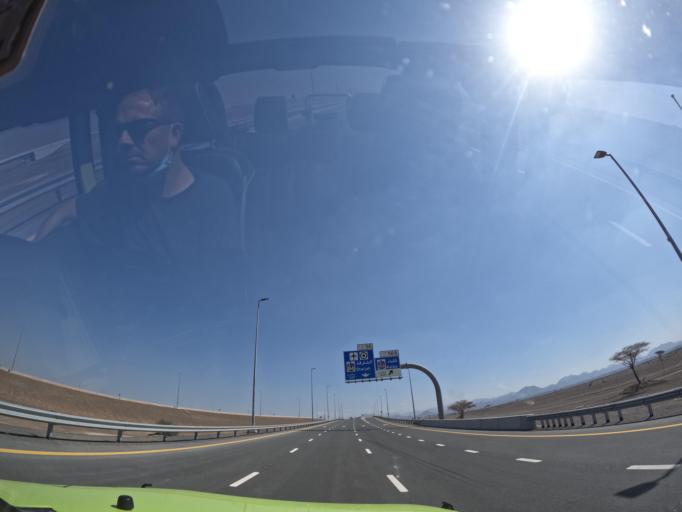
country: AE
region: Ash Shariqah
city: Adh Dhayd
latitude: 25.1169
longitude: 55.9446
